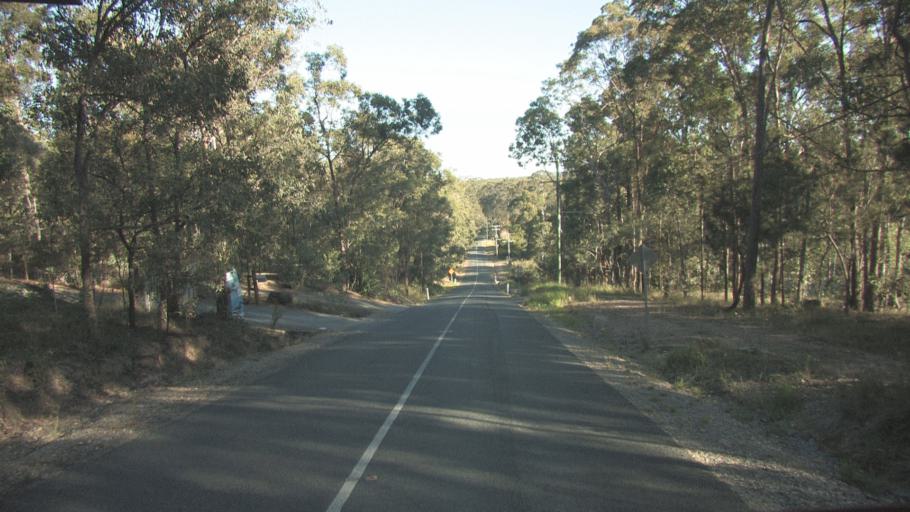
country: AU
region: Queensland
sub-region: Logan
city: Chambers Flat
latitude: -27.7646
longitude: 153.1227
